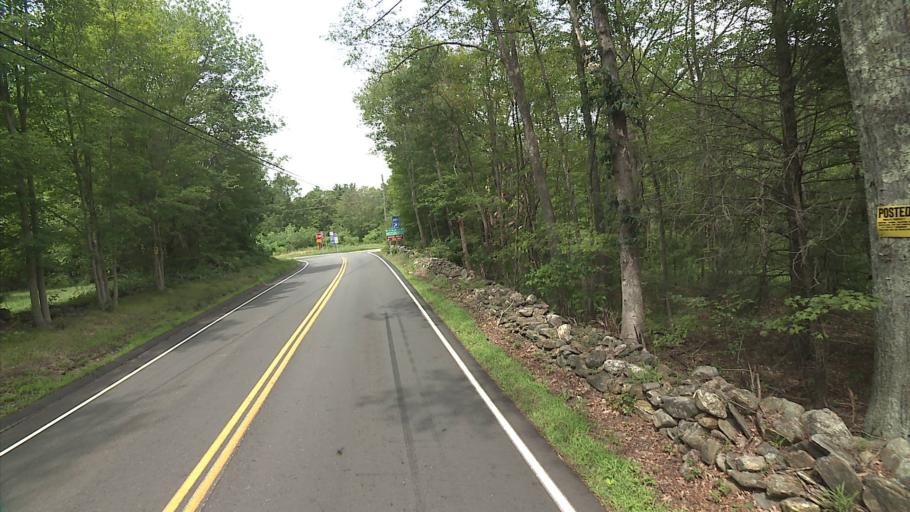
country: US
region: Massachusetts
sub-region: Hampden County
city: Holland
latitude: 41.9838
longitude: -72.1161
